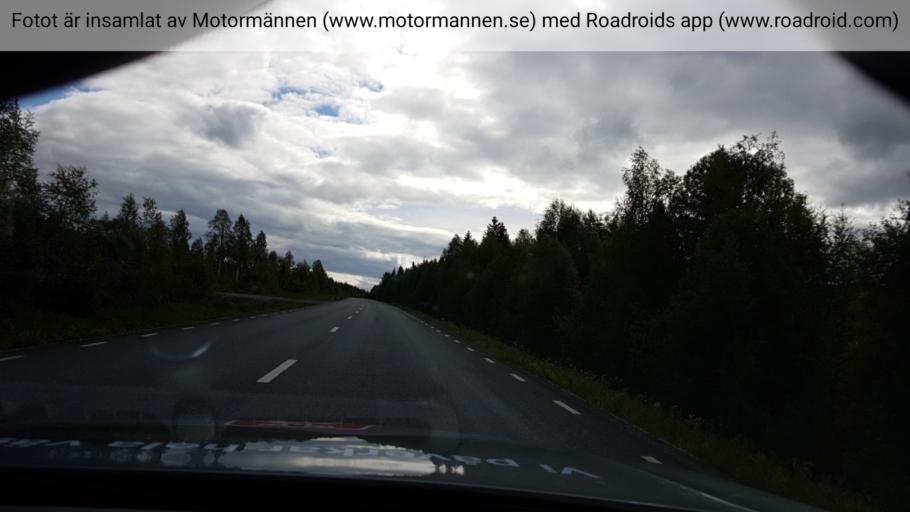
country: SE
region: Jaemtland
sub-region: Stroemsunds Kommun
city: Stroemsund
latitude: 64.1186
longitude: 15.6224
